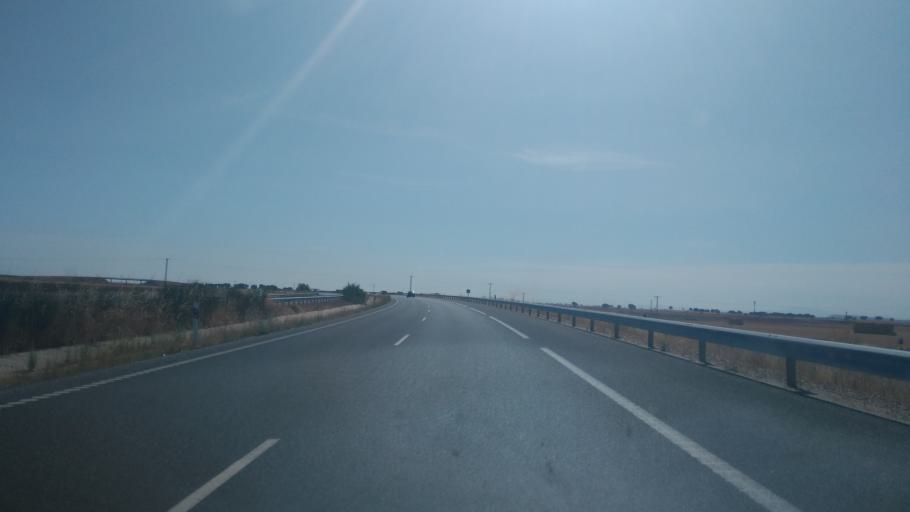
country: ES
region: Castille and Leon
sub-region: Provincia de Salamanca
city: Pelabravo
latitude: 40.9297
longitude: -5.5862
